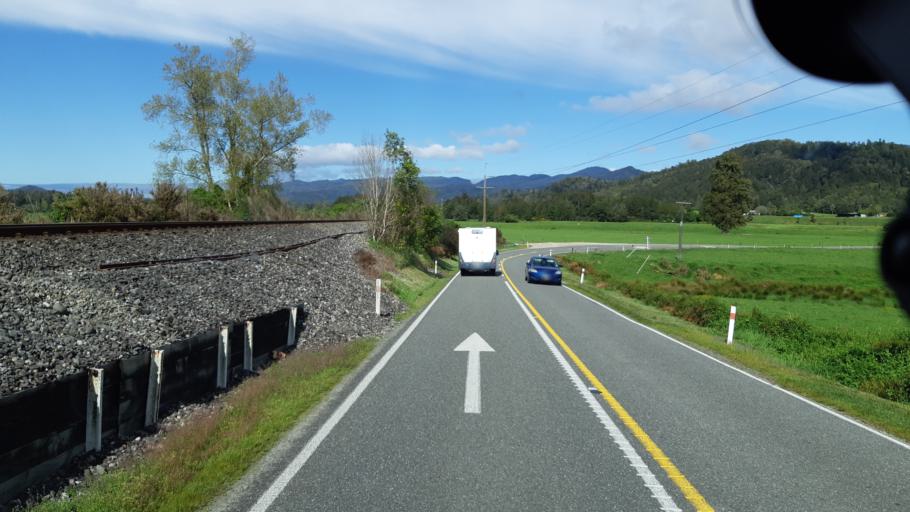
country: NZ
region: West Coast
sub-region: Buller District
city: Westport
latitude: -41.8607
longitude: 171.9441
